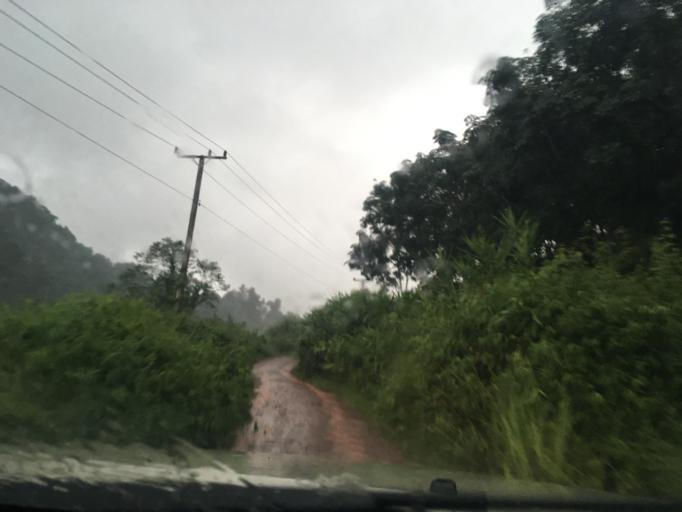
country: LA
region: Oudomxai
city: Muang La
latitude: 21.2418
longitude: 101.9445
